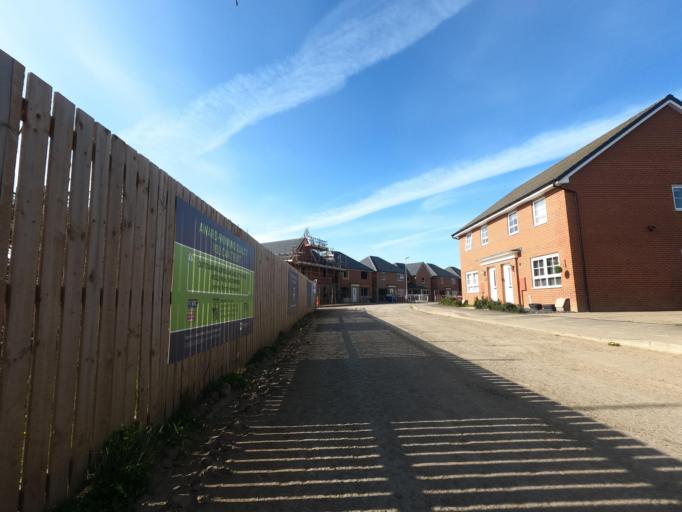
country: GB
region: England
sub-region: Northumberland
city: Morpeth
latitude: 55.1567
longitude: -1.6686
